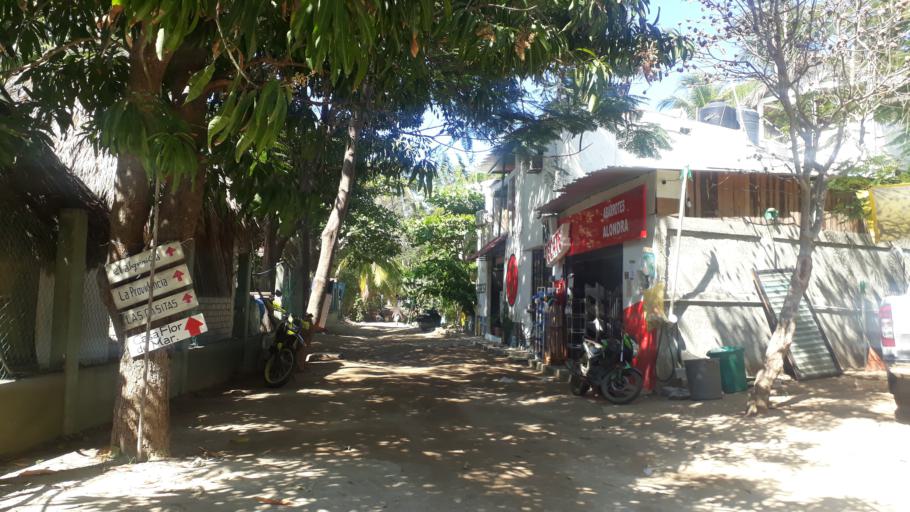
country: MX
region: Oaxaca
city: Santa Maria Tonameca
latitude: 15.6643
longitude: -96.5214
